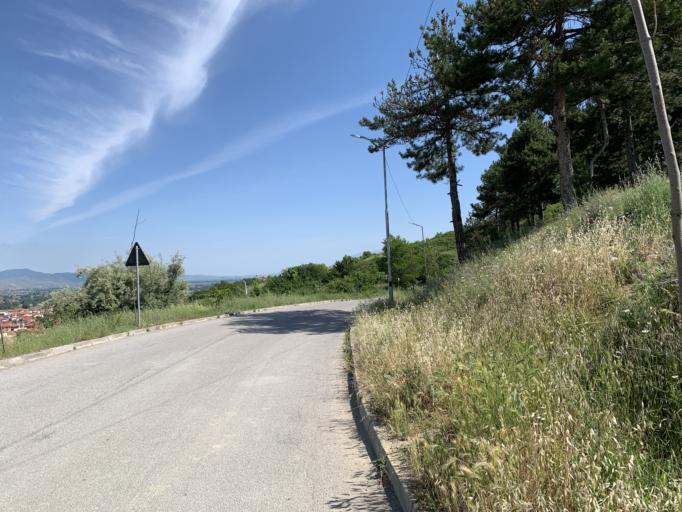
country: AL
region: Korce
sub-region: Rrethi i Korces
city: Korce
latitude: 40.6160
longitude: 20.7876
